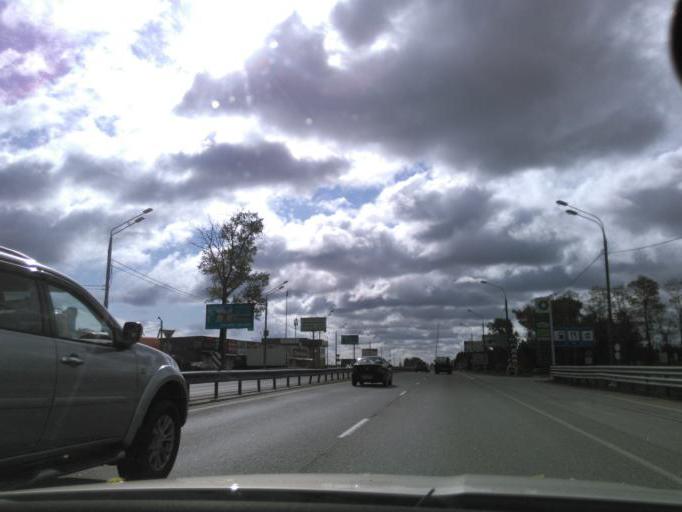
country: RU
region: Moskovskaya
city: Rzhavki
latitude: 55.9962
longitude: 37.2535
